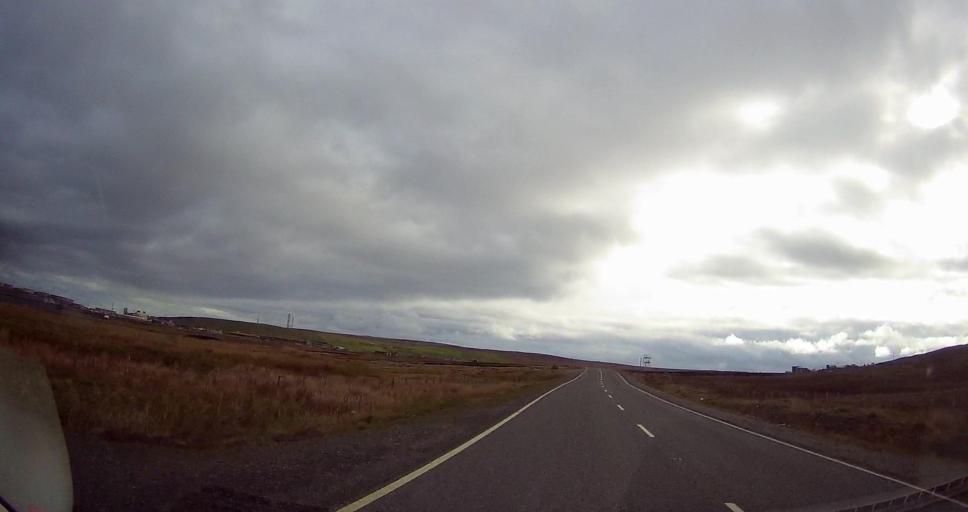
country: GB
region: Scotland
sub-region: Shetland Islands
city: Lerwick
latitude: 60.4368
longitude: -1.2804
